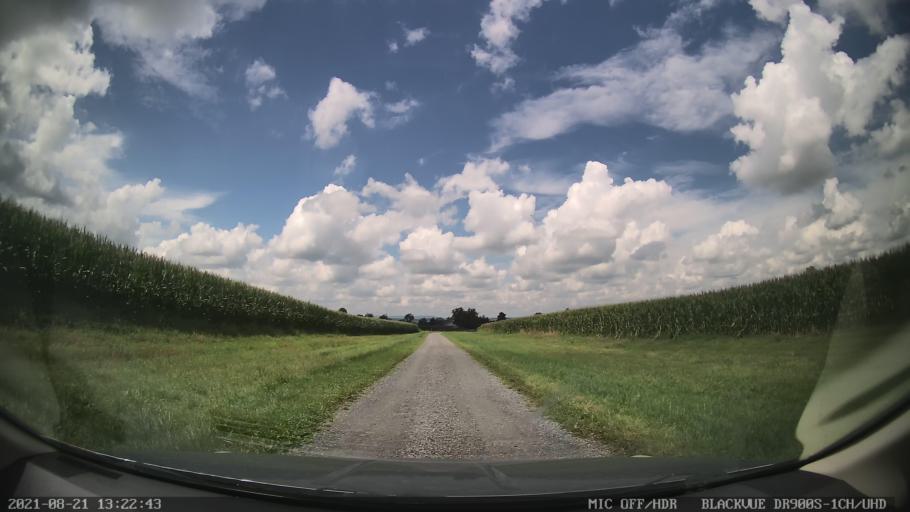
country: US
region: Pennsylvania
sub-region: Berks County
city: Fleetwood
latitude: 40.4682
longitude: -75.7787
